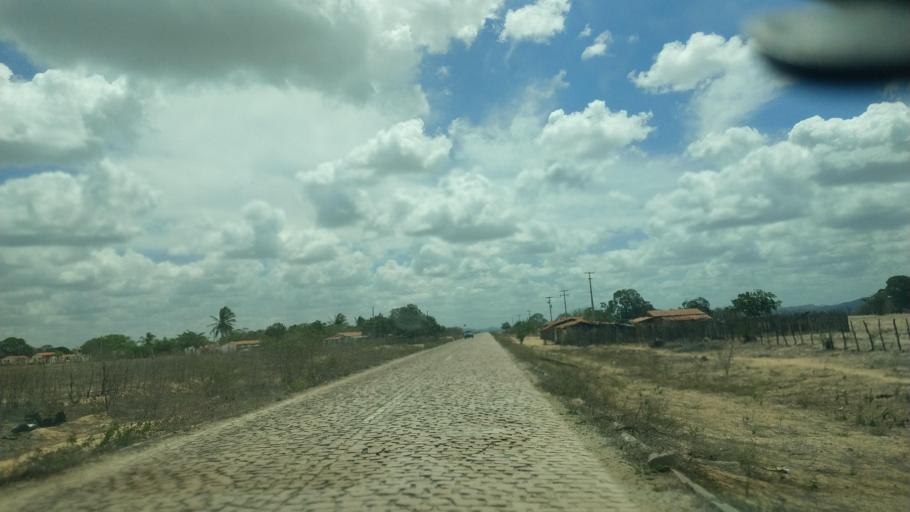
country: BR
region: Rio Grande do Norte
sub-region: Sao Paulo Do Potengi
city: Sao Paulo do Potengi
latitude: -5.9788
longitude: -35.8569
